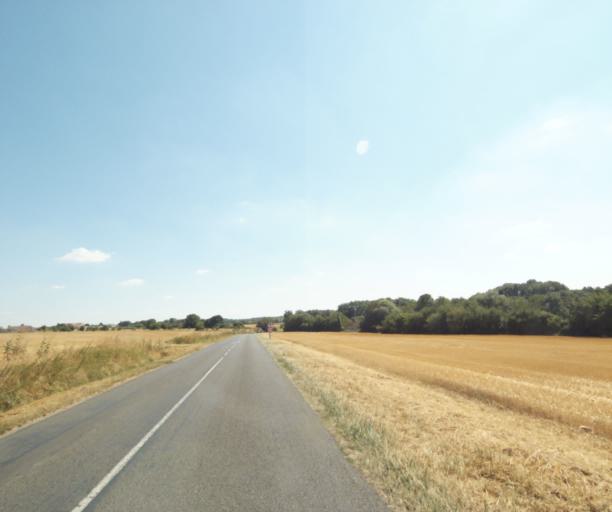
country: FR
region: Ile-de-France
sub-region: Departement de Seine-et-Marne
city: Conches-sur-Gondoire
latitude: 48.8583
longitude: 2.7274
